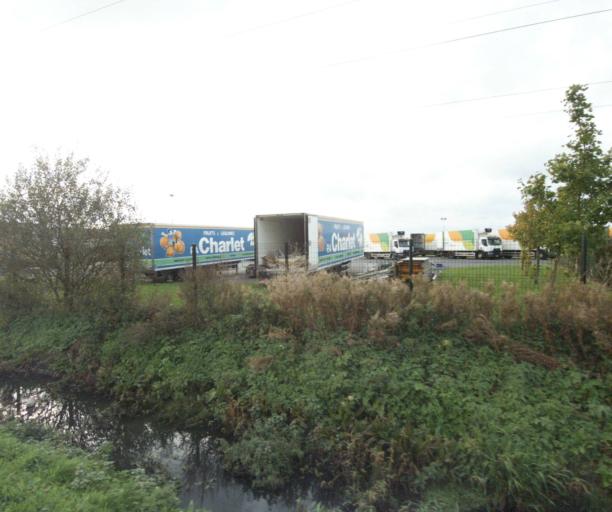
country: FR
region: Nord-Pas-de-Calais
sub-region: Departement du Nord
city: Bois-Grenier
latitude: 50.6523
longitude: 2.8969
